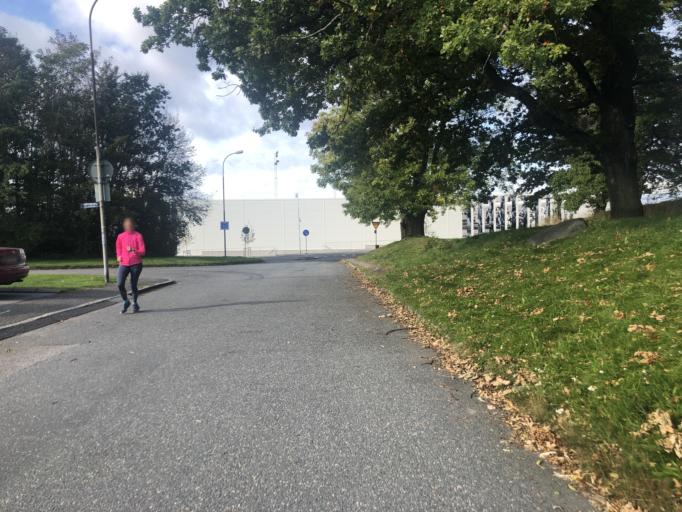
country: SE
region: Vaestra Goetaland
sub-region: Molndal
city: Moelndal
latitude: 57.6503
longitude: 12.0064
